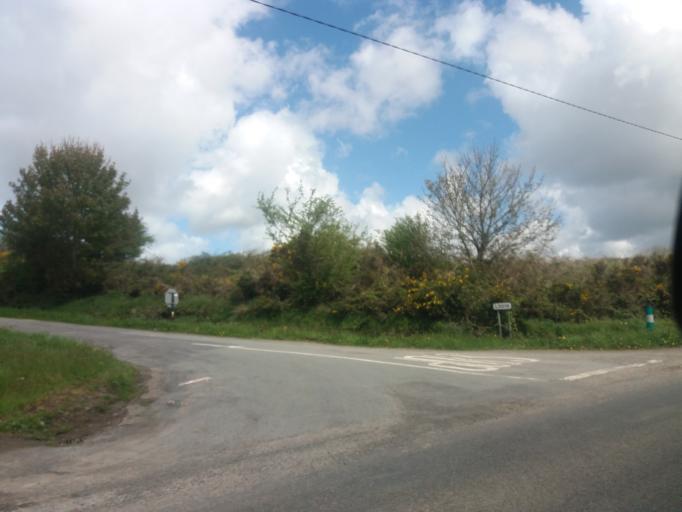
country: IE
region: Leinster
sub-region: Loch Garman
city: Loch Garman
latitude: 52.2899
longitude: -6.5907
